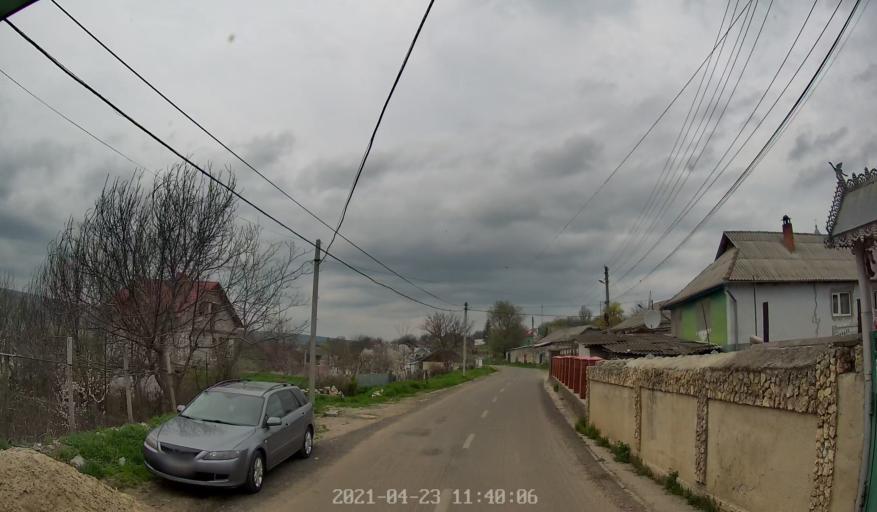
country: MD
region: Chisinau
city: Vadul lui Voda
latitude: 47.1181
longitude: 29.0490
